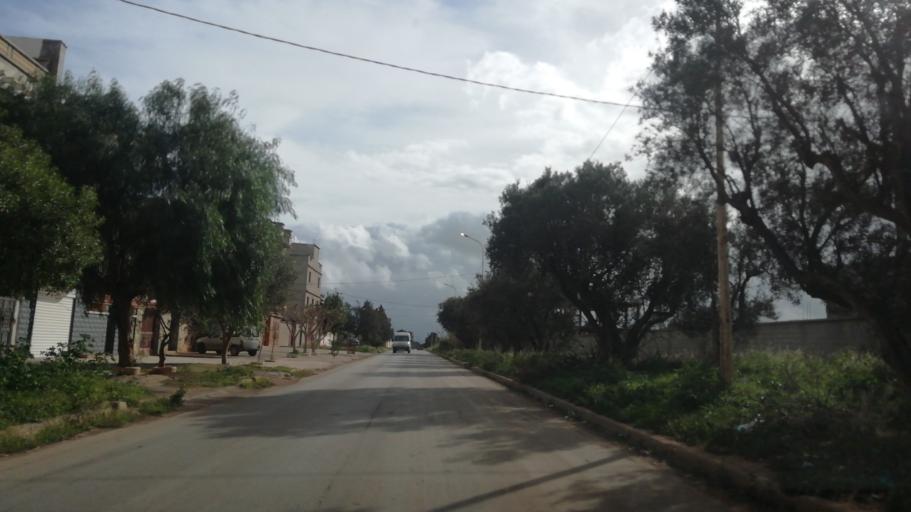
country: DZ
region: Oran
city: Es Senia
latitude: 35.6594
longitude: -0.6380
